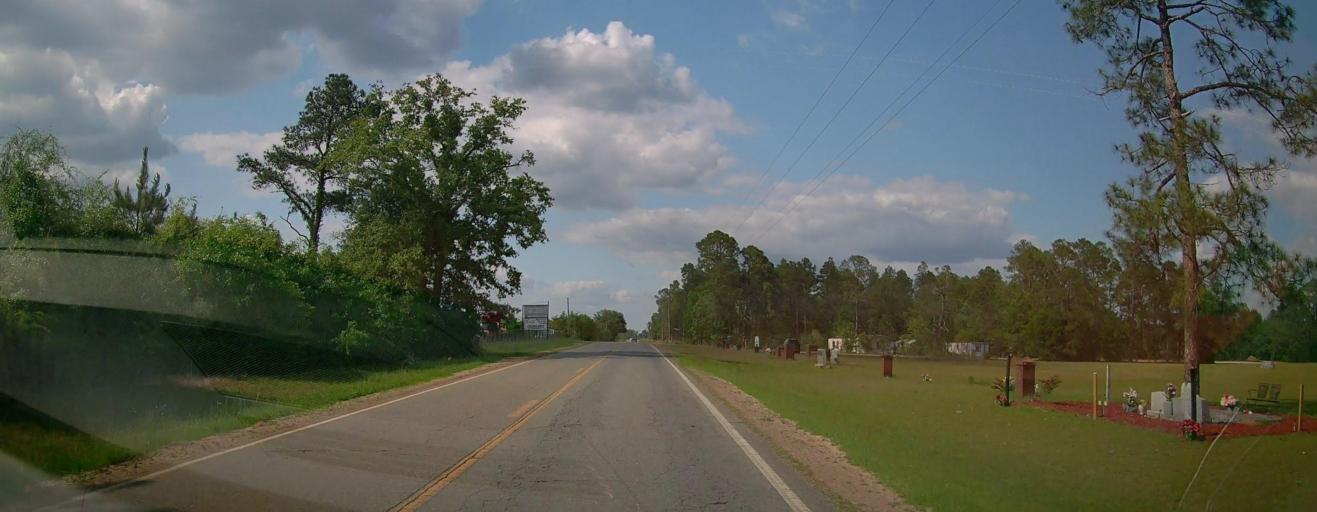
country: US
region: Georgia
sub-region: Laurens County
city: East Dublin
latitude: 32.5849
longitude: -82.8644
